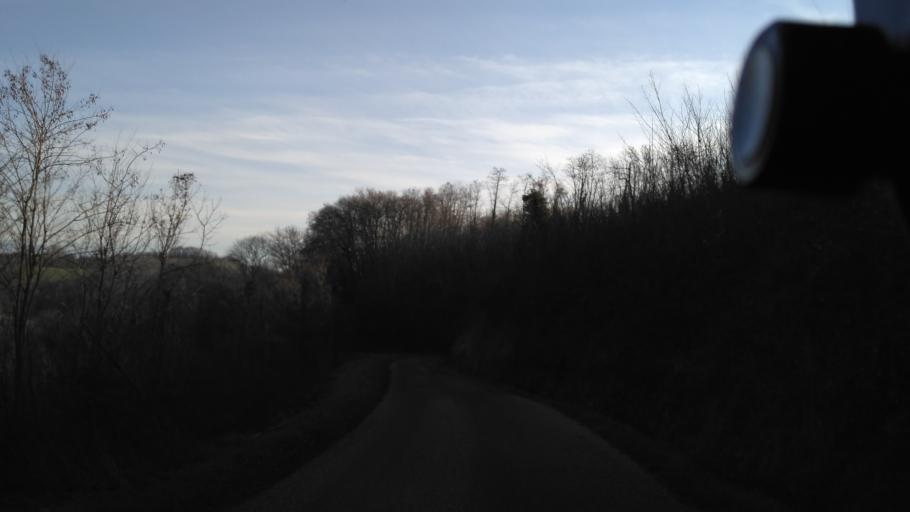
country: FR
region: Rhone-Alpes
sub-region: Departement de l'Isere
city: Saint-Lattier
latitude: 45.1336
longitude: 5.1492
